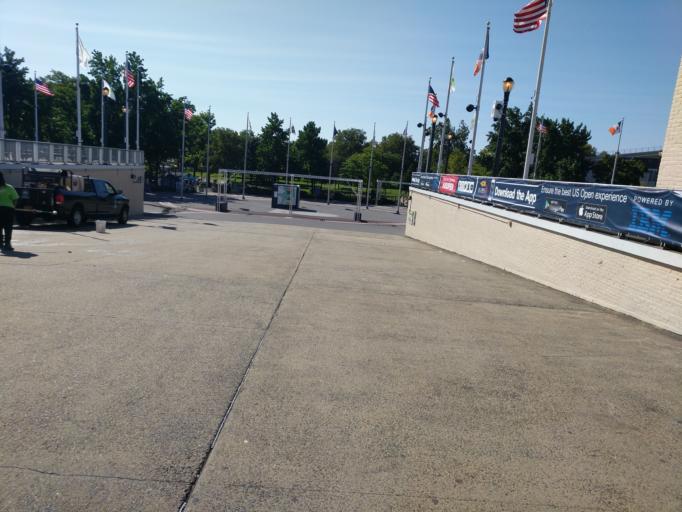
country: US
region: New York
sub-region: Queens County
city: Borough of Queens
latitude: 40.7518
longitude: -73.8434
